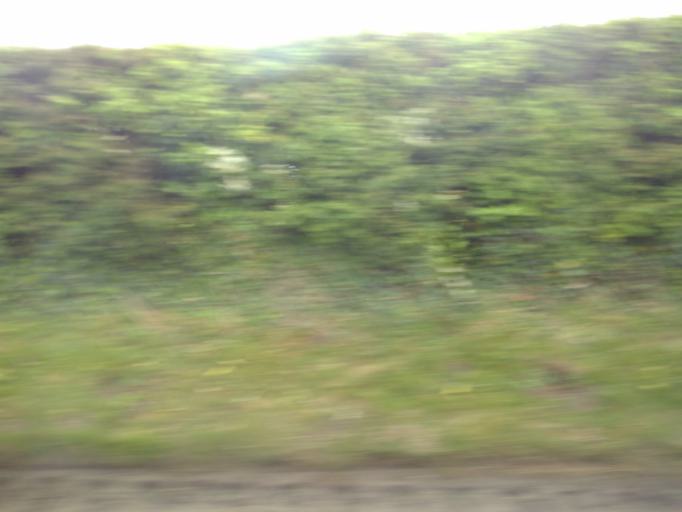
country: GB
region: England
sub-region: Norfolk
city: Sheringham
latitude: 52.9441
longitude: 1.1106
